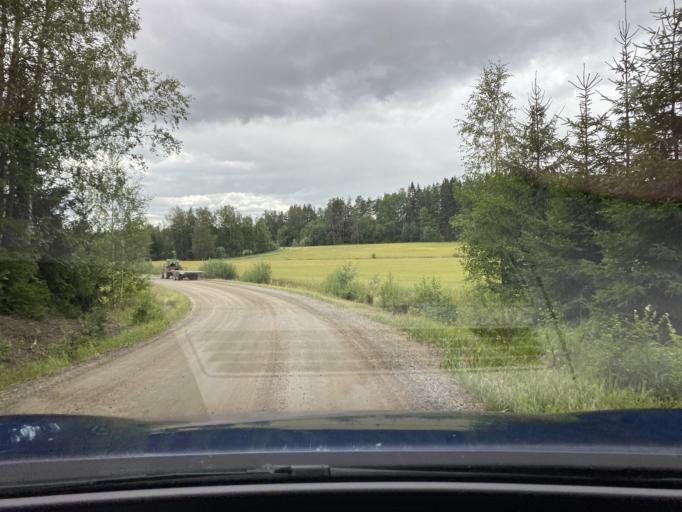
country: FI
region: Pirkanmaa
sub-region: Lounais-Pirkanmaa
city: Punkalaidun
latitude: 61.1740
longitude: 23.1802
